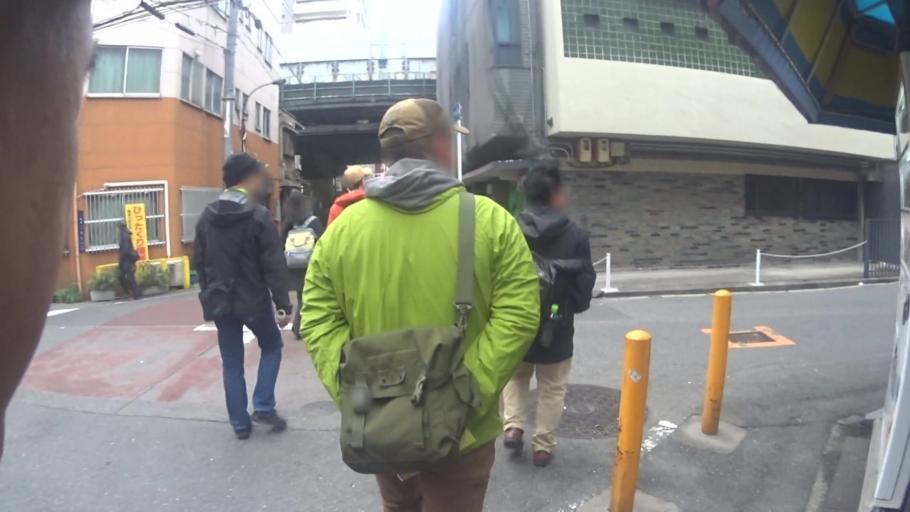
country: JP
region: Osaka
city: Osaka-shi
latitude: 34.6653
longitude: 135.5113
